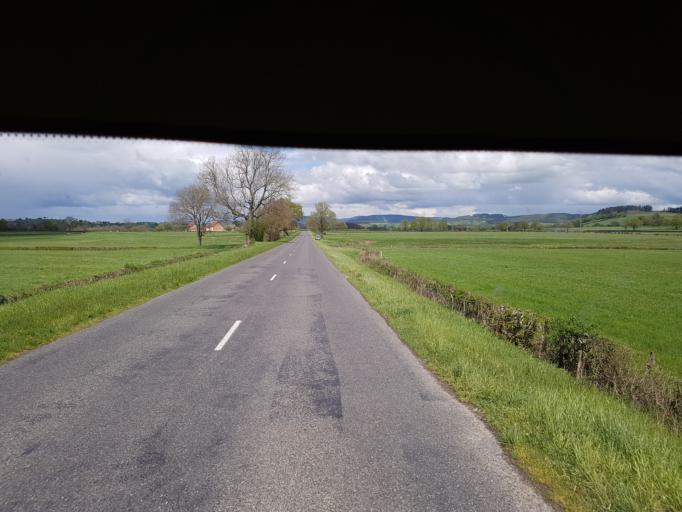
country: FR
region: Bourgogne
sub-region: Departement de Saone-et-Loire
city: Etang-sur-Arroux
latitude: 46.8135
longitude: 4.1614
